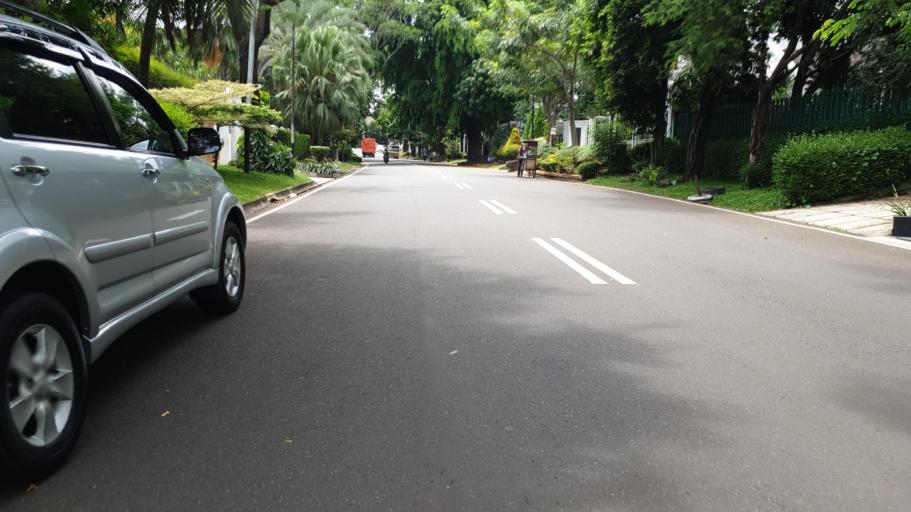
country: ID
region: Banten
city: South Tangerang
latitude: -6.2796
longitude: 106.7846
